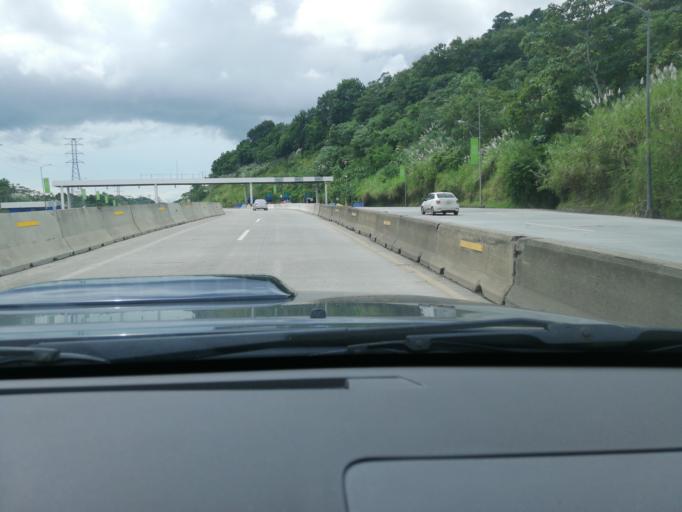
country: PA
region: Panama
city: San Miguelito
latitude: 9.0778
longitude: -79.4626
